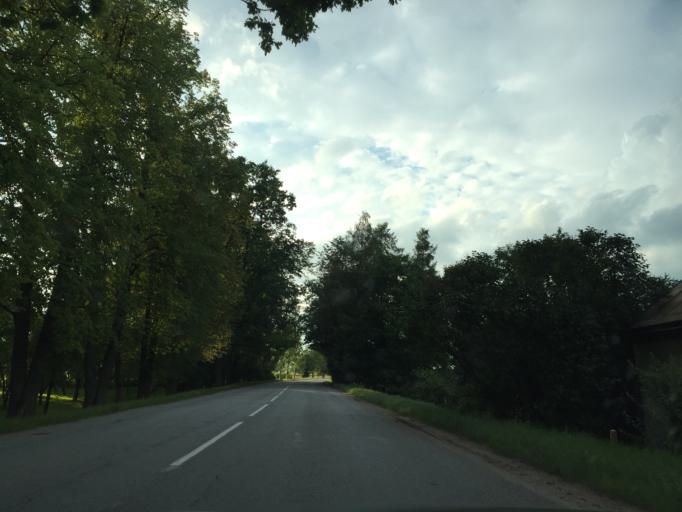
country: LV
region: Dobeles Rajons
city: Dobele
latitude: 56.7433
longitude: 23.3929
